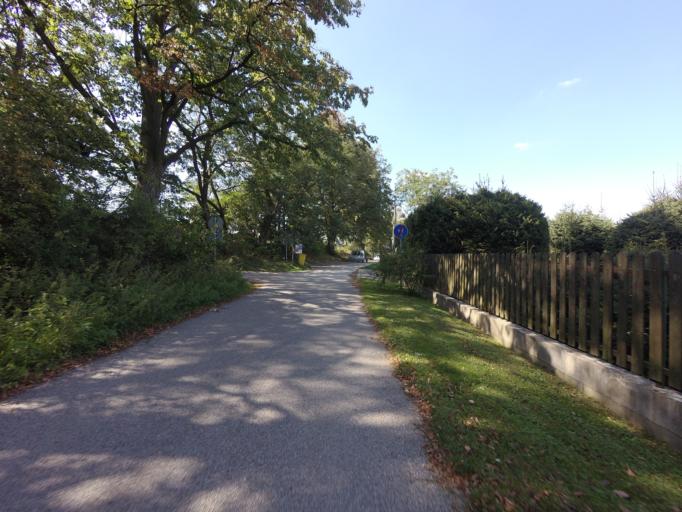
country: CZ
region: Jihocesky
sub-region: Okres Ceske Budejovice
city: Hluboka nad Vltavou
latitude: 49.1232
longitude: 14.4558
